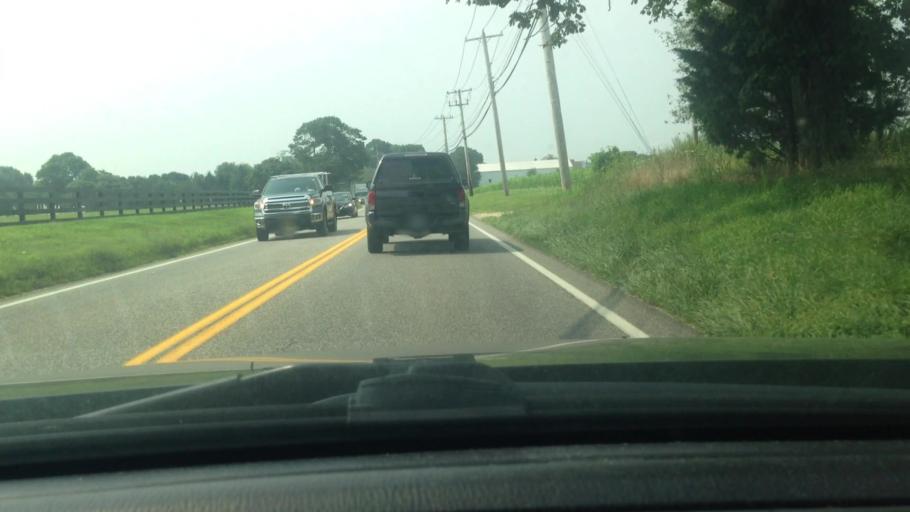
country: US
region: New York
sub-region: Suffolk County
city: Water Mill
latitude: 40.9422
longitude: -72.3353
